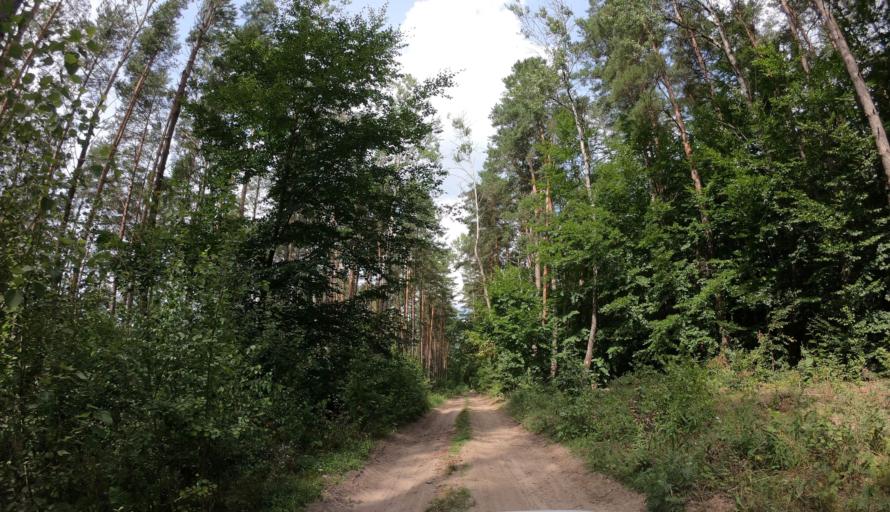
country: PL
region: West Pomeranian Voivodeship
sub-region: Powiat gryfinski
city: Stare Czarnowo
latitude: 53.3326
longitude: 14.8068
